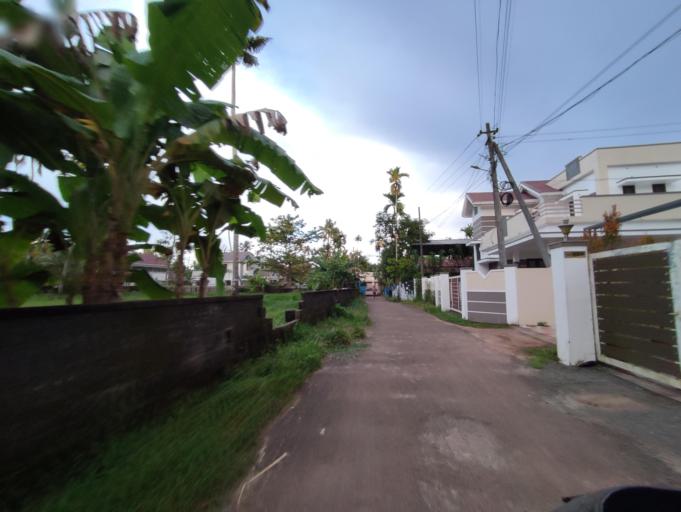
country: IN
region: Kerala
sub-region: Alappuzha
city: Vayalar
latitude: 9.6957
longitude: 76.3346
